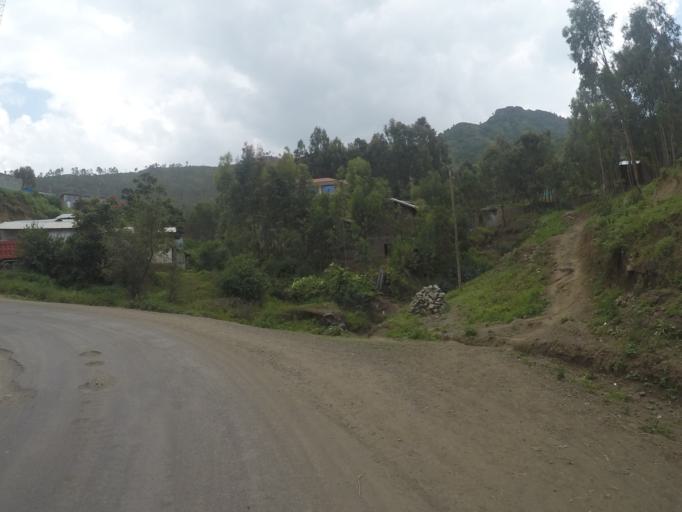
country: ET
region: Amhara
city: Lalibela
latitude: 12.0278
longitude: 39.0496
